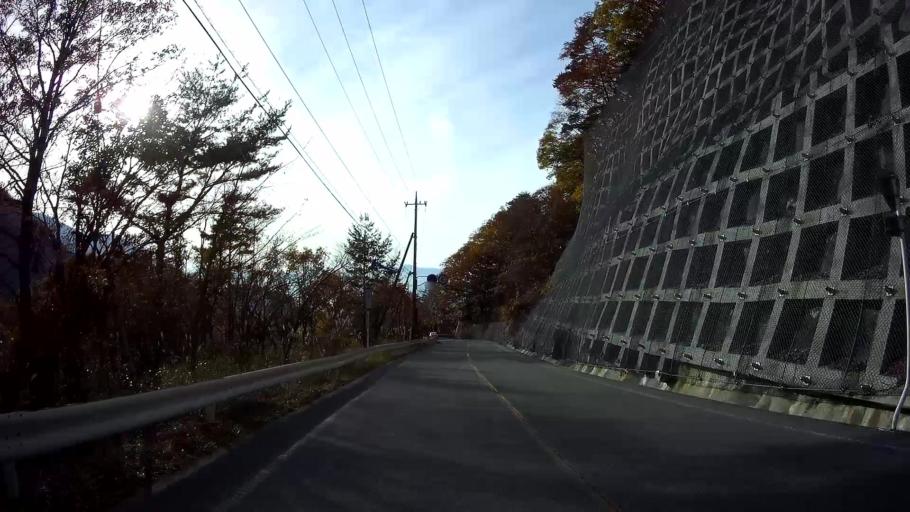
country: JP
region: Yamanashi
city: Fujikawaguchiko
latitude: 35.4774
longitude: 138.5671
